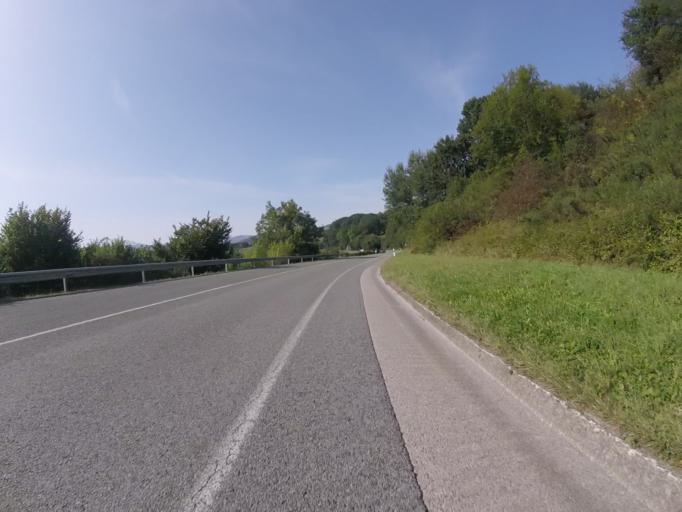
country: ES
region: Navarre
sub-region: Provincia de Navarra
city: Zugarramurdi
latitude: 43.1942
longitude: -1.4842
